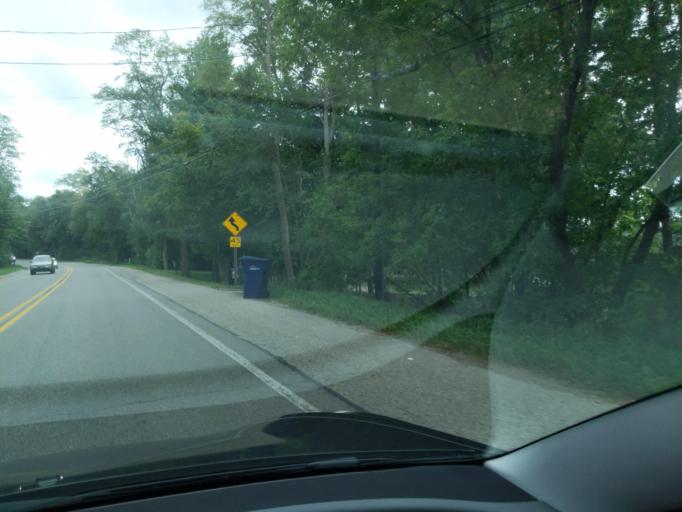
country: US
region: Michigan
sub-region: Kalkaska County
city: Rapid City
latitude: 44.8743
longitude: -85.2790
